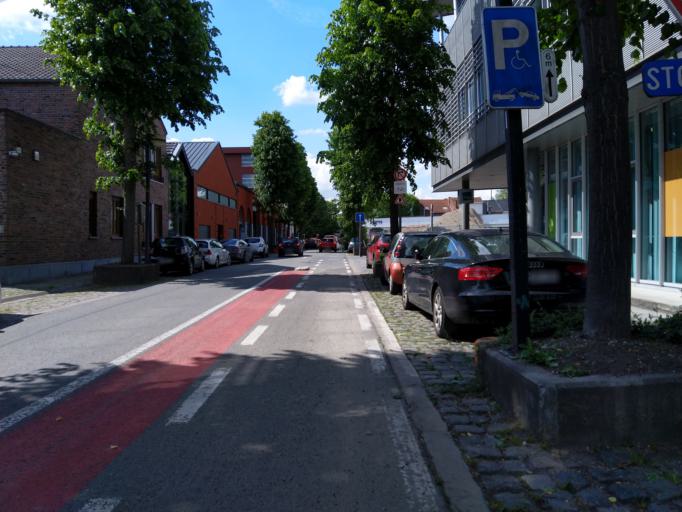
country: BE
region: Wallonia
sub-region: Province du Hainaut
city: Mons
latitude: 50.4496
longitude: 3.9420
